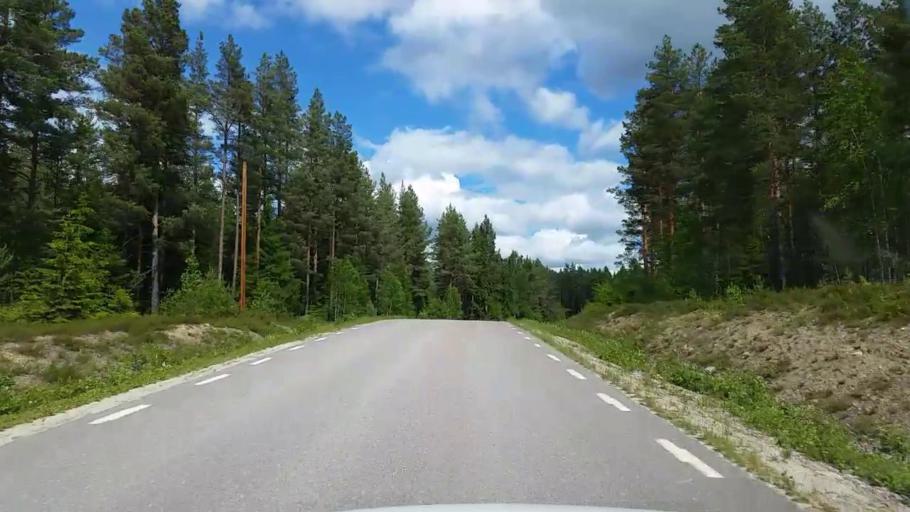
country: SE
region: Gaevleborg
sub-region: Ovanakers Kommun
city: Alfta
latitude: 61.4055
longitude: 16.0547
